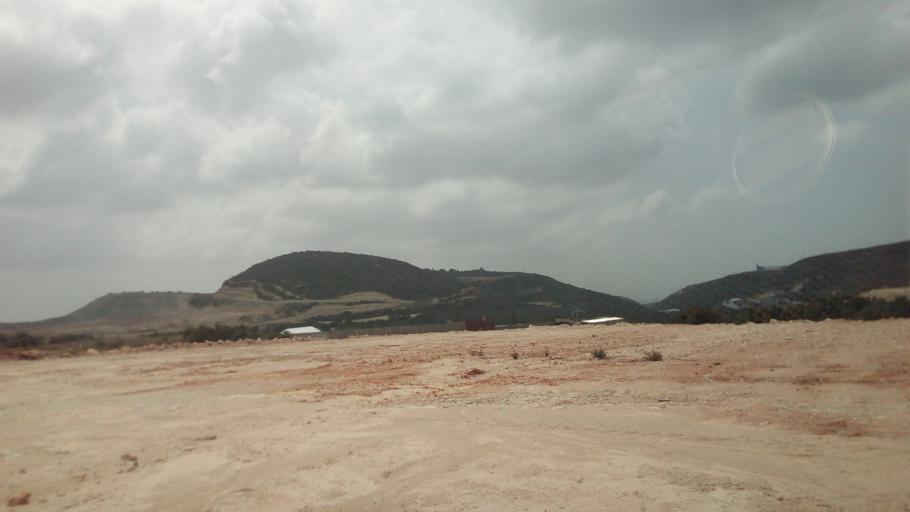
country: CY
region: Limassol
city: Ypsonas
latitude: 34.7528
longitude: 32.9420
